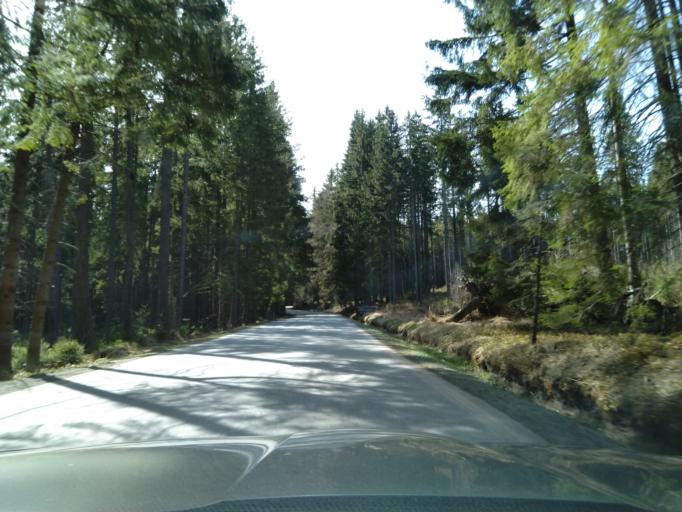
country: CZ
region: Jihocesky
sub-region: Okres Prachatice
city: Stachy
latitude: 49.0585
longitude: 13.6561
